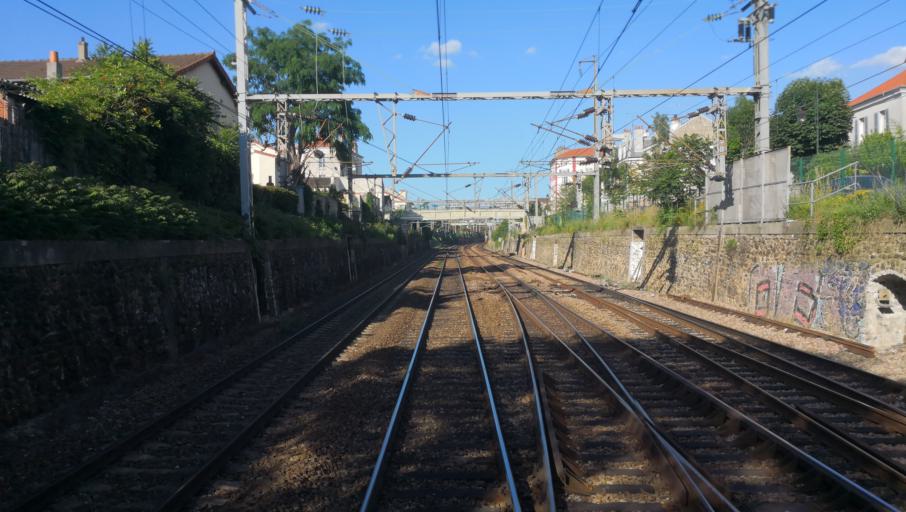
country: FR
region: Ile-de-France
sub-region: Departement des Hauts-de-Seine
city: La Garenne-Colombes
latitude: 48.9116
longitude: 2.2455
